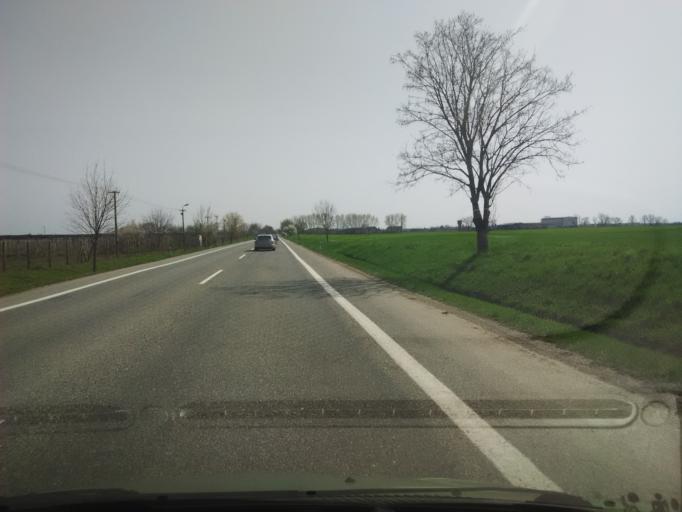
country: SK
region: Nitriansky
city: Surany
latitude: 48.1110
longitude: 18.0474
